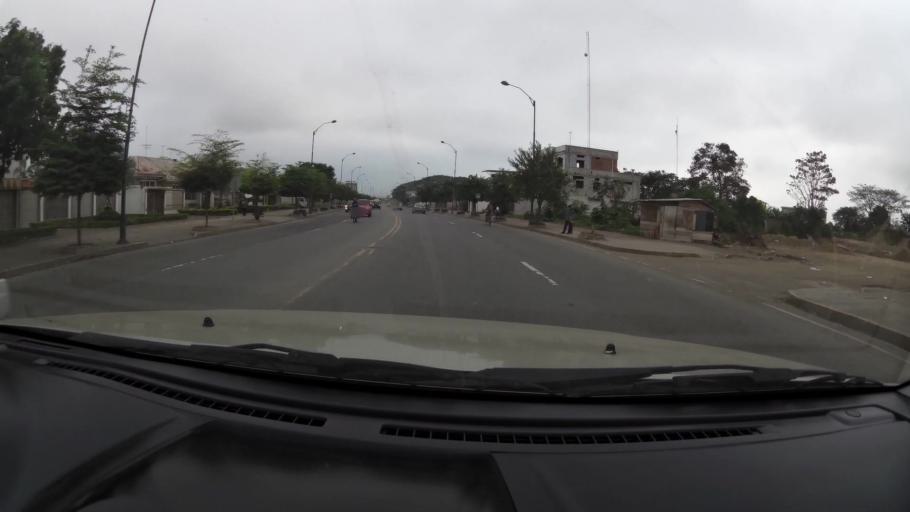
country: EC
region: El Oro
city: Machala
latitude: -3.2809
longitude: -79.9395
